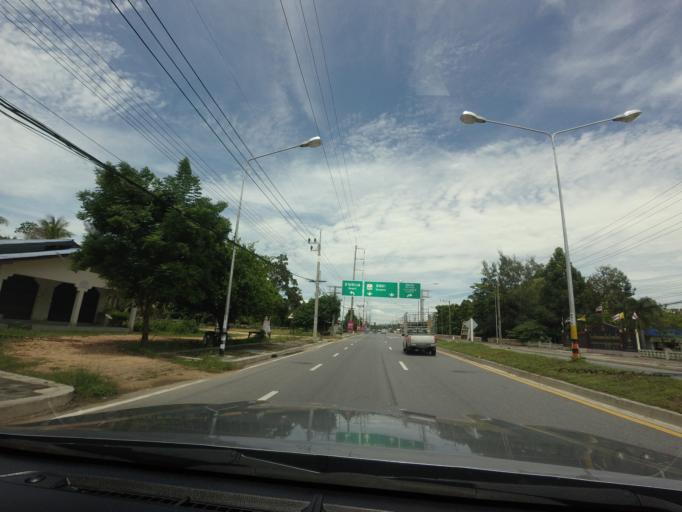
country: TH
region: Songkhla
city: Krasae Sin
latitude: 7.6035
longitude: 100.4004
